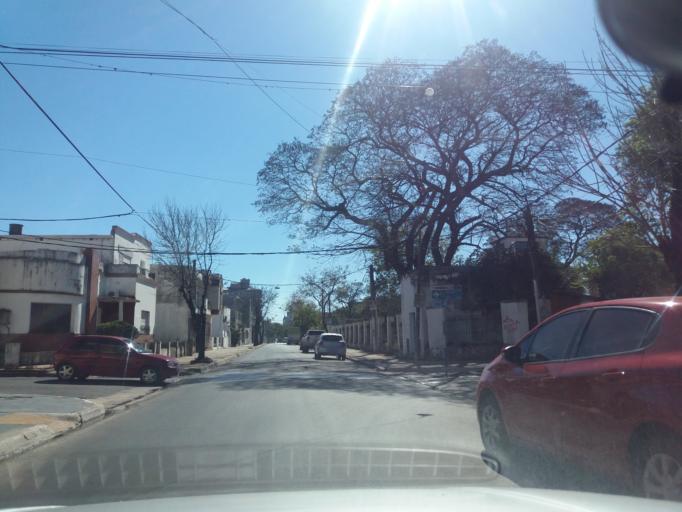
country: AR
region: Corrientes
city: Corrientes
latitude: -27.4730
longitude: -58.8410
